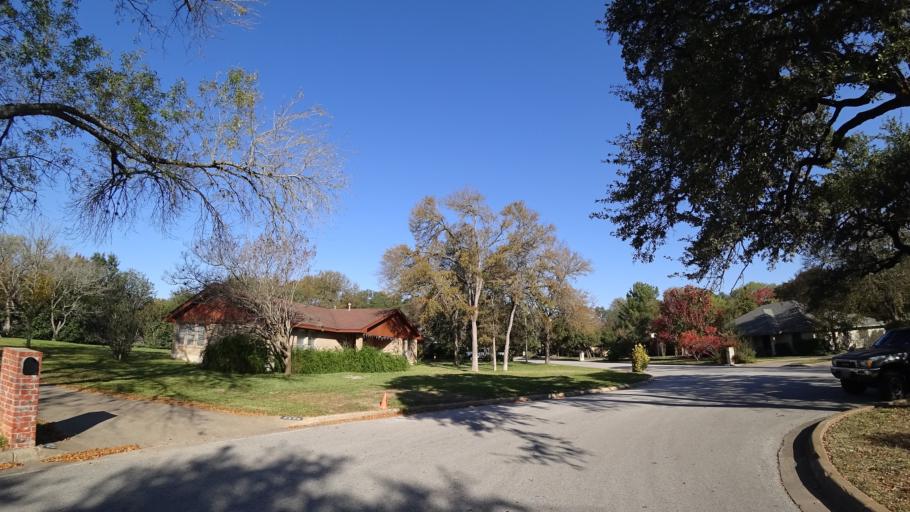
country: US
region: Texas
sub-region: Travis County
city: Shady Hollow
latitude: 30.2198
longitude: -97.8474
